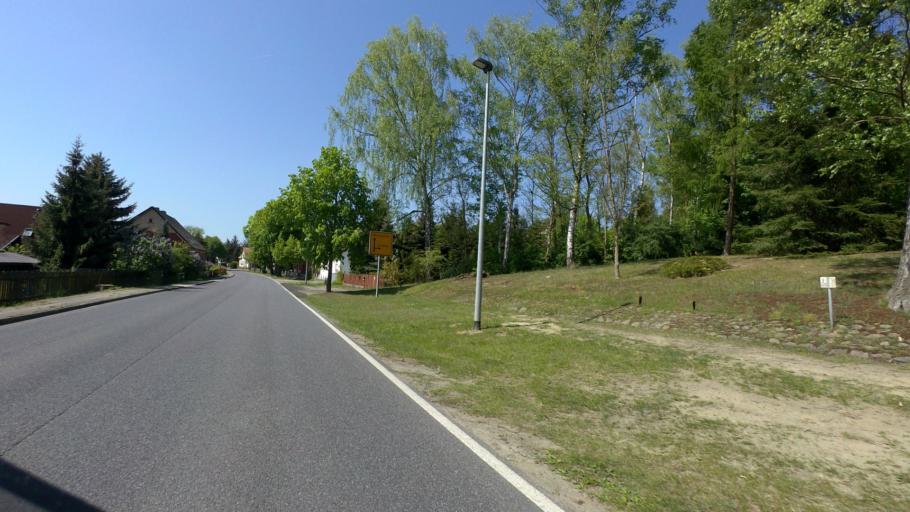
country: DE
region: Brandenburg
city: Jamlitz
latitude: 51.9911
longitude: 14.3574
